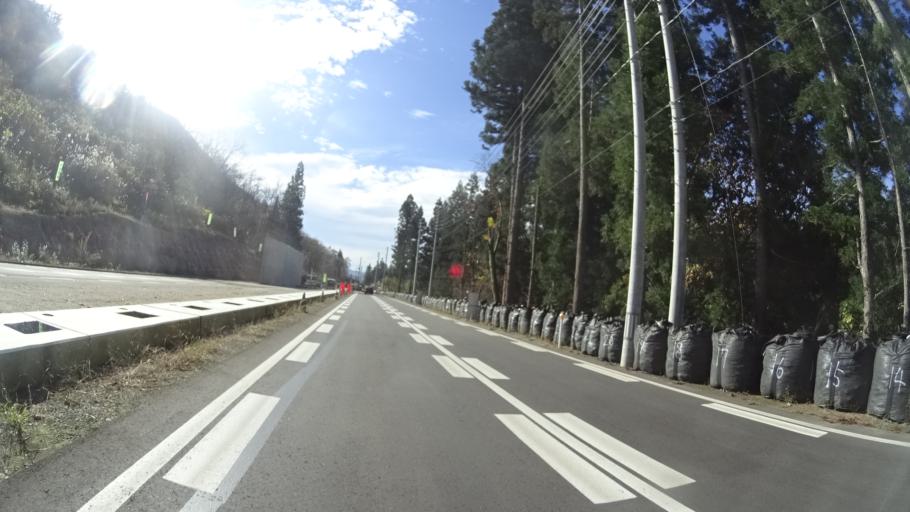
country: JP
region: Niigata
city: Ojiya
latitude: 37.2718
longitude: 138.9873
